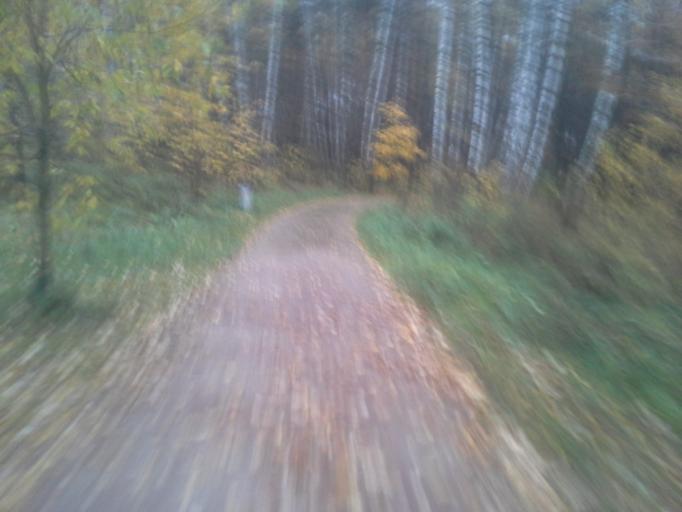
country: RU
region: Moskovskaya
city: Zarech'ye
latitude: 55.6665
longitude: 37.3845
